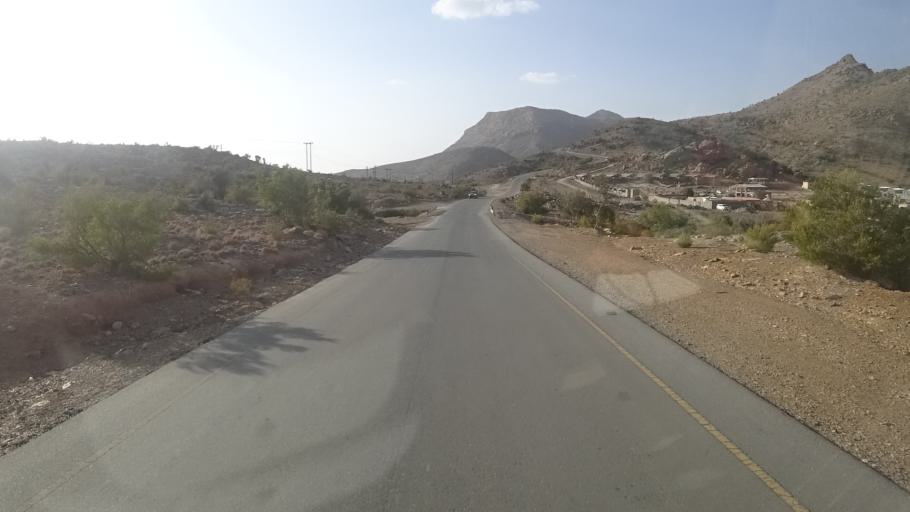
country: OM
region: Muhafazat ad Dakhiliyah
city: Bahla'
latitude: 23.2248
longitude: 57.2029
